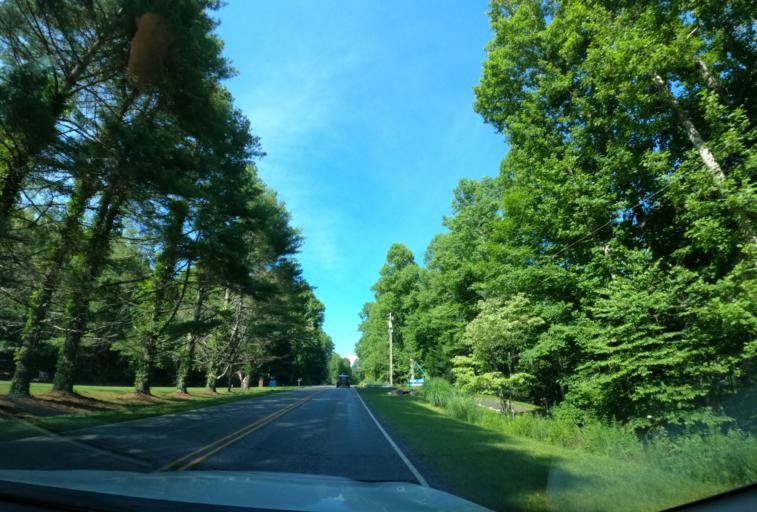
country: US
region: North Carolina
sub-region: Henderson County
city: Etowah
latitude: 35.2228
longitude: -82.6106
